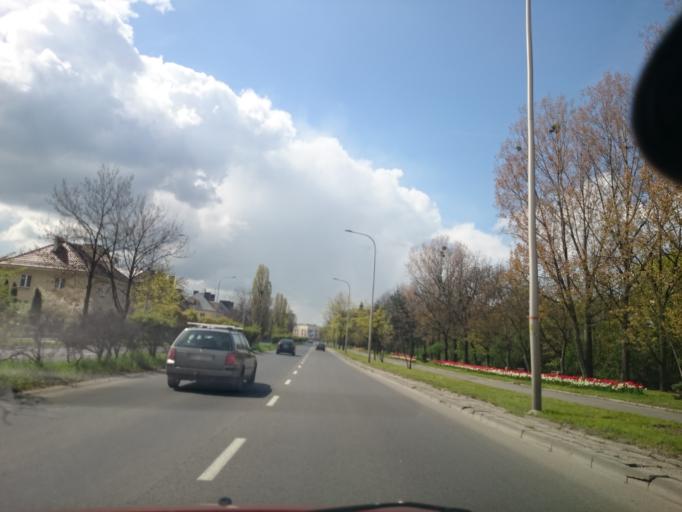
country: PL
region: Opole Voivodeship
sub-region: Powiat opolski
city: Opole
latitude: 50.6755
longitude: 17.9290
